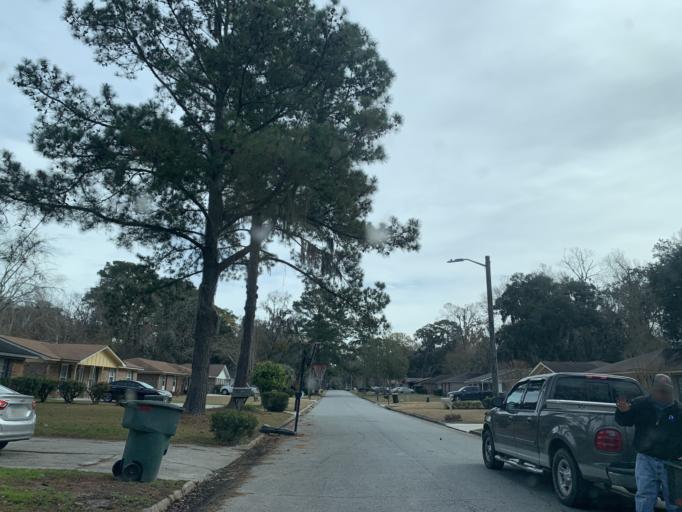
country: US
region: Georgia
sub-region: Chatham County
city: Montgomery
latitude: 31.9684
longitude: -81.1325
